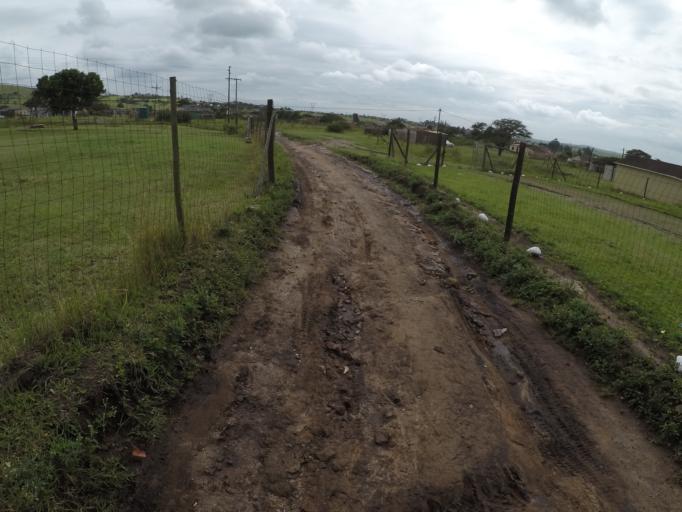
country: ZA
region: KwaZulu-Natal
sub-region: uThungulu District Municipality
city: Empangeni
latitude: -28.7135
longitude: 31.8592
